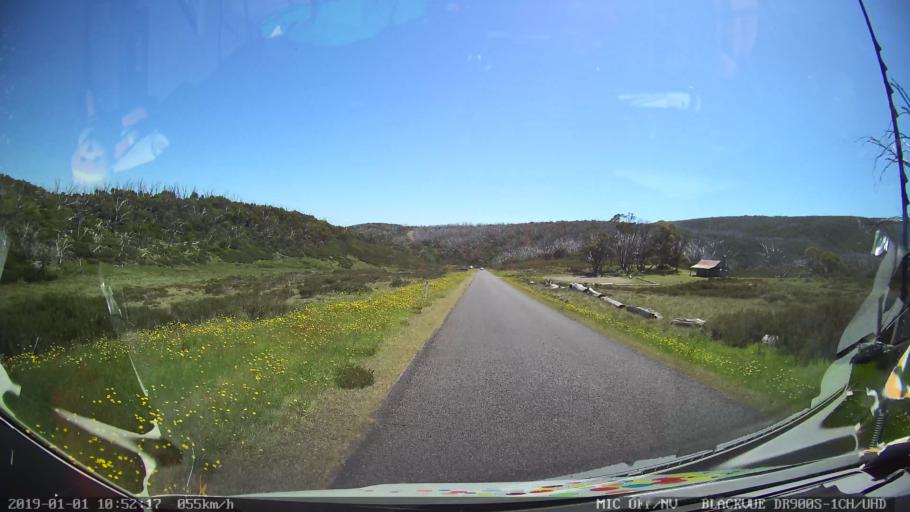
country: AU
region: New South Wales
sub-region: Snowy River
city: Jindabyne
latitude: -36.0164
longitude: 148.3785
